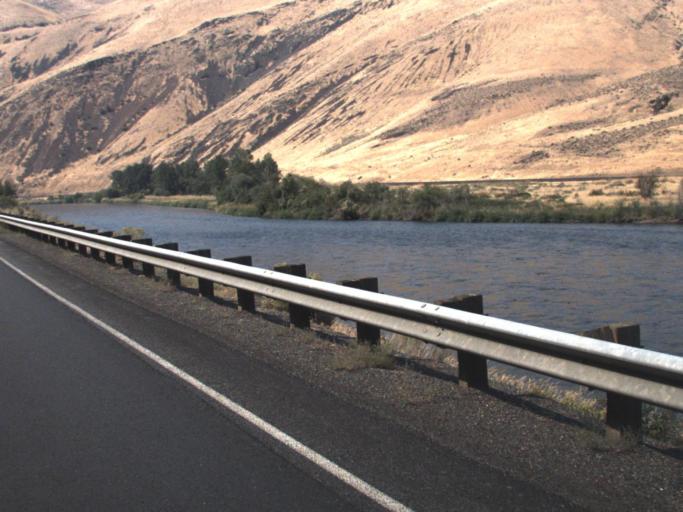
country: US
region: Washington
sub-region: Yakima County
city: Selah
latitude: 46.8006
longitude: -120.4512
